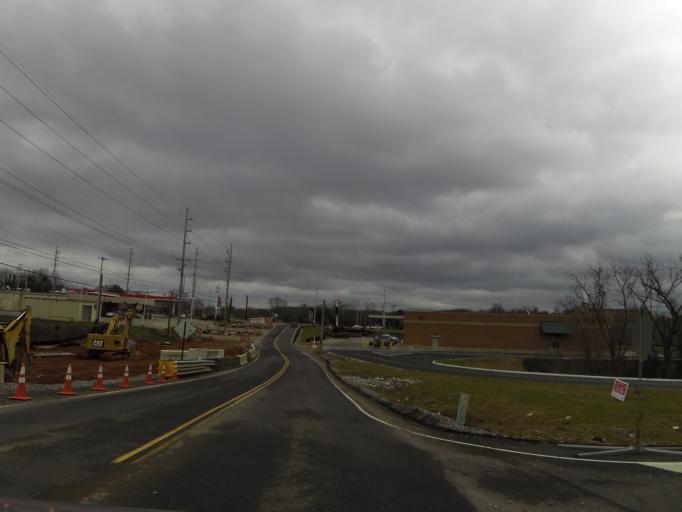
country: US
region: Tennessee
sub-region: Union County
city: Condon
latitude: 36.1207
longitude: -83.8554
